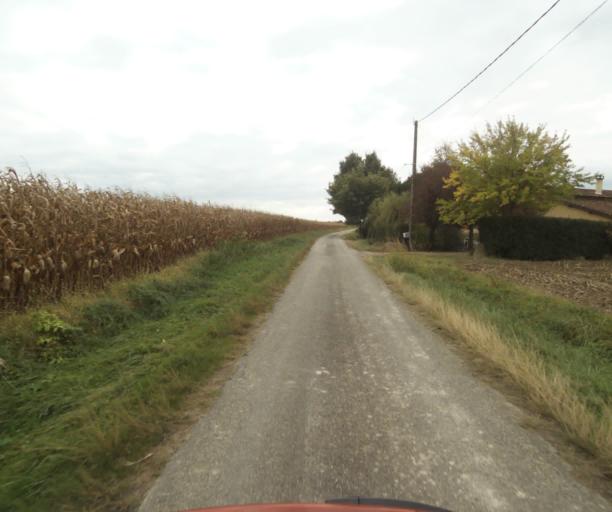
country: FR
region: Midi-Pyrenees
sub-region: Departement du Tarn-et-Garonne
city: Finhan
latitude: 43.8939
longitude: 1.2631
